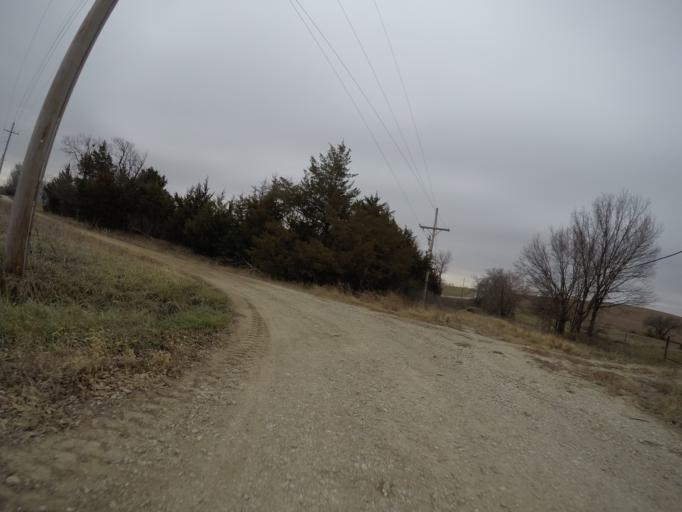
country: US
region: Kansas
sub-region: Wabaunsee County
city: Alma
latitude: 38.8555
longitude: -96.1133
